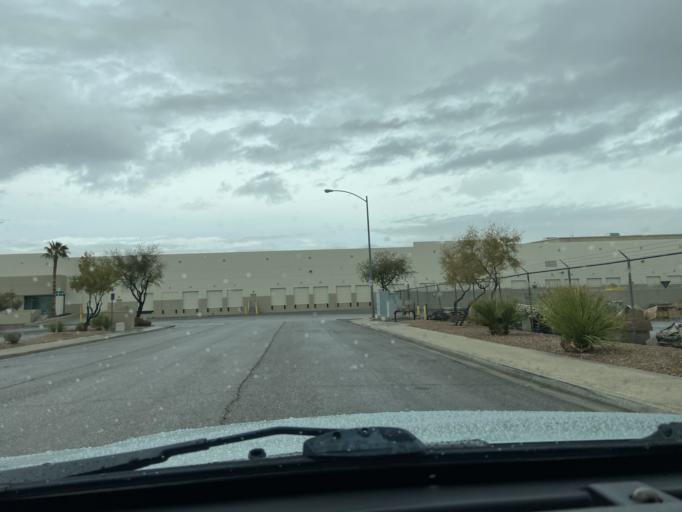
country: US
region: Nevada
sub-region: Clark County
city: Sunrise Manor
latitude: 36.2355
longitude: -115.1004
